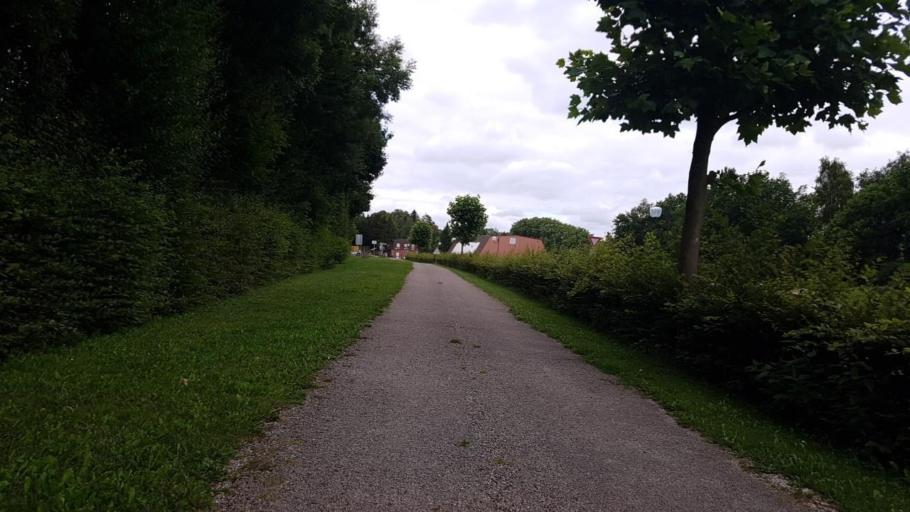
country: FR
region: Picardie
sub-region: Departement de l'Aisne
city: Hirson
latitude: 49.9107
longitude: 4.0620
